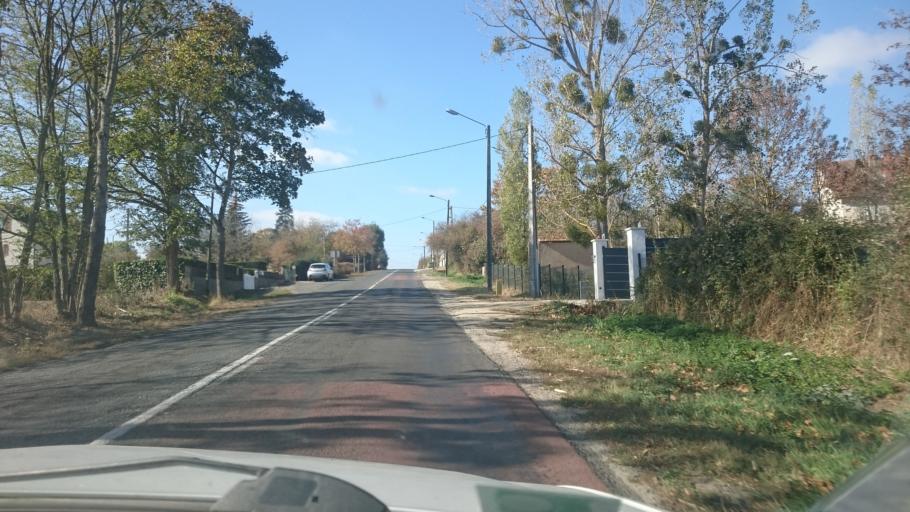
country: FR
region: Auvergne
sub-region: Departement de l'Allier
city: Neuvy
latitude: 46.5562
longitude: 3.2919
